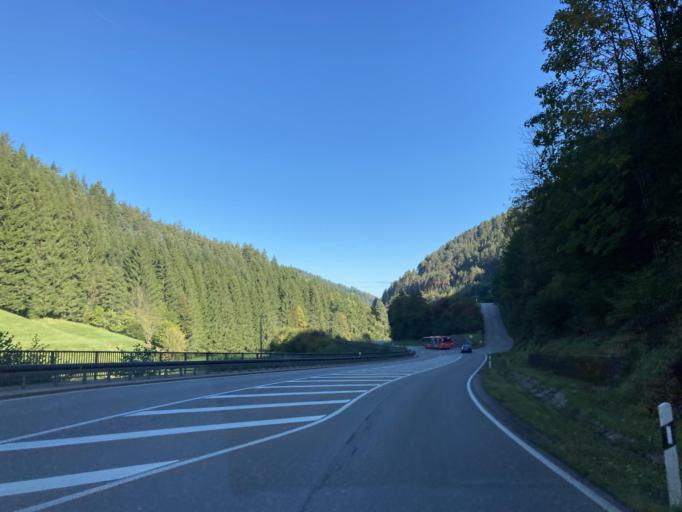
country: DE
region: Baden-Wuerttemberg
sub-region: Freiburg Region
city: Hornberg
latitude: 48.1822
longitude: 8.2310
